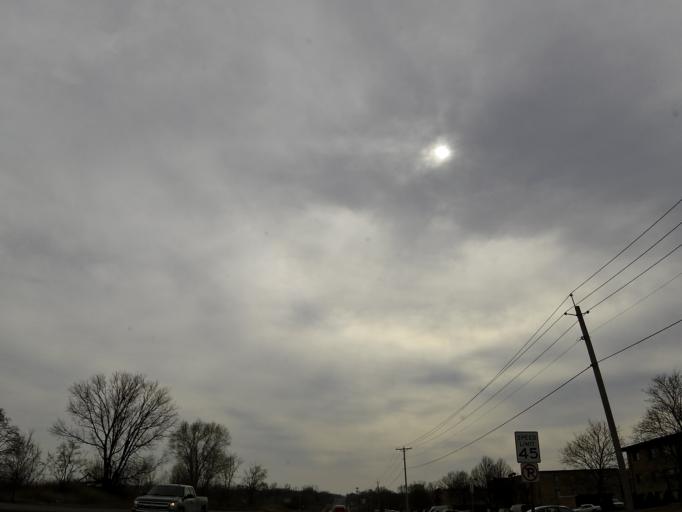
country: US
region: Minnesota
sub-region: Dakota County
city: Inver Grove Heights
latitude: 44.8471
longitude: -93.0207
